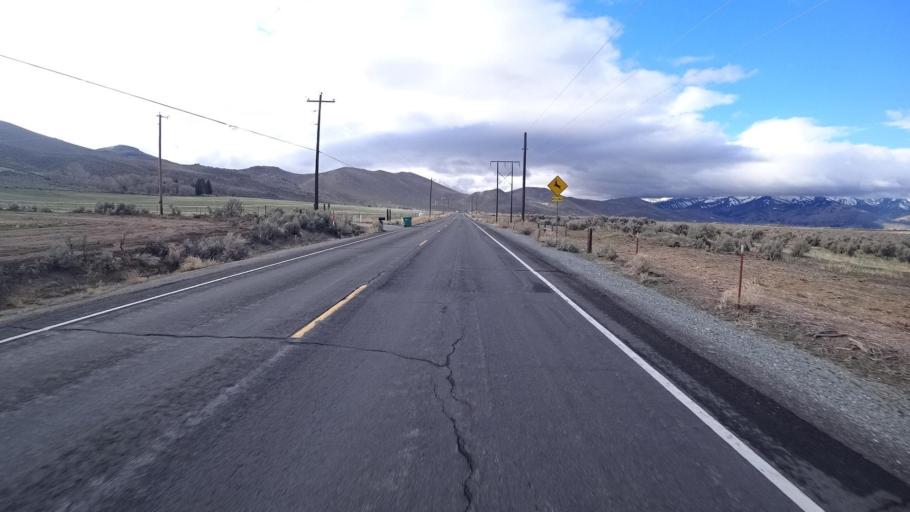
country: US
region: Nevada
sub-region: Carson City
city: Carson City
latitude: 39.2588
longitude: -119.7565
